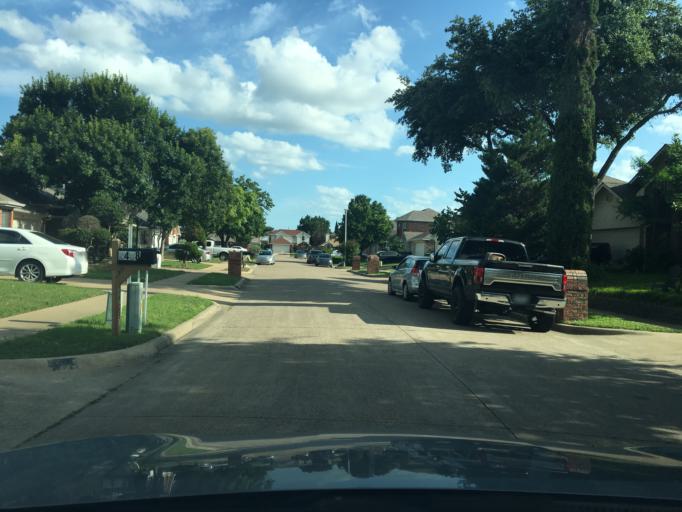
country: US
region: Texas
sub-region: Dallas County
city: Garland
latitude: 32.9375
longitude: -96.6802
